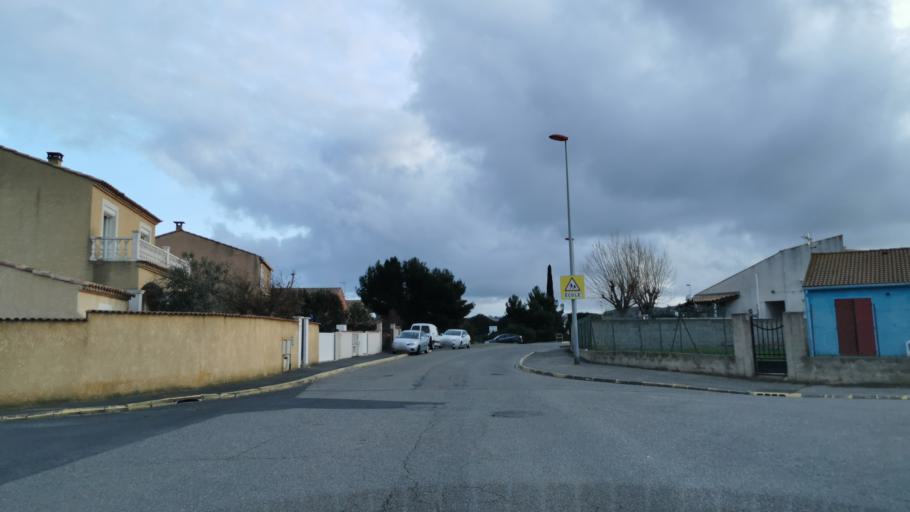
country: FR
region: Languedoc-Roussillon
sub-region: Departement de l'Aude
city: Narbonne
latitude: 43.1869
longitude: 2.9754
